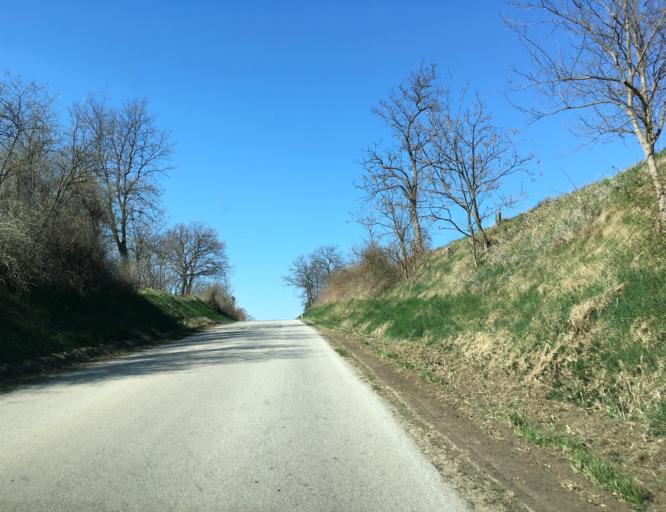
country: HU
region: Komarom-Esztergom
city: Nyergesujfalu
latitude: 47.8246
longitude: 18.6025
